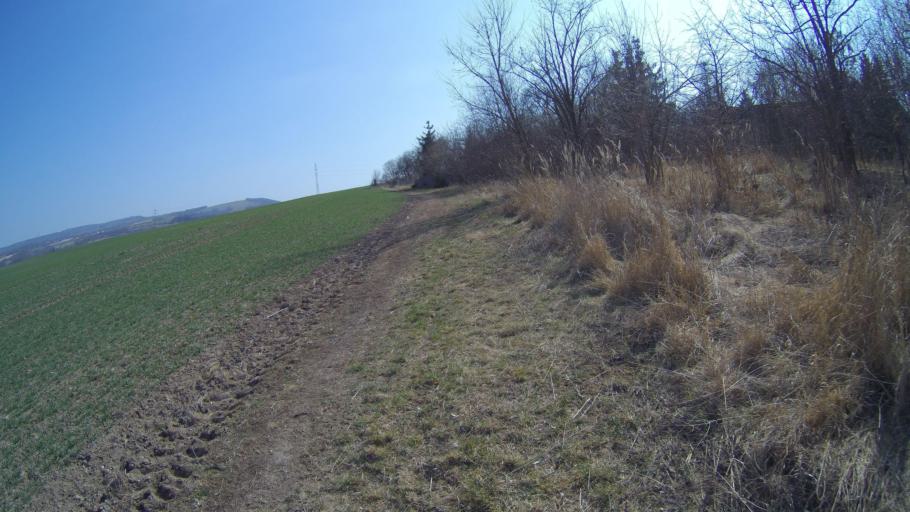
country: CZ
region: Ustecky
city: Mecholupy
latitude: 50.2901
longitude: 13.5797
